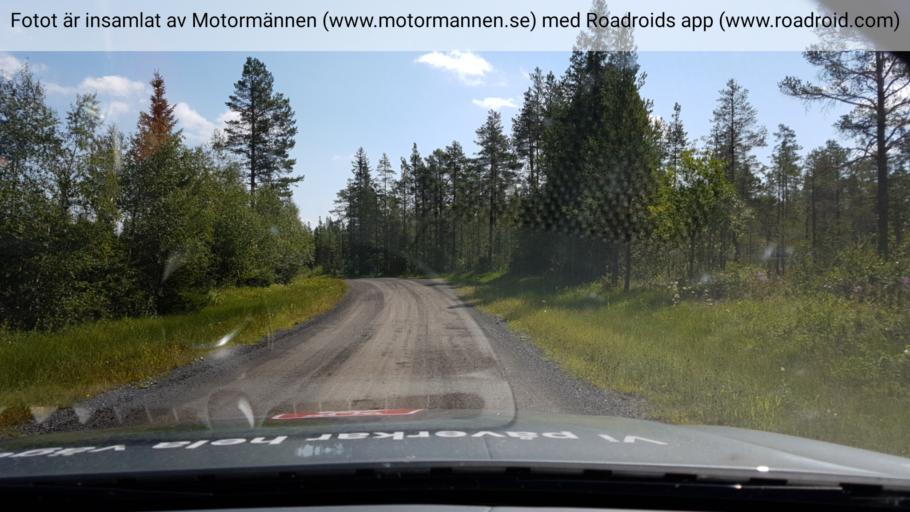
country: SE
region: Jaemtland
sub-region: OEstersunds Kommun
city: Lit
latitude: 63.3497
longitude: 15.3469
